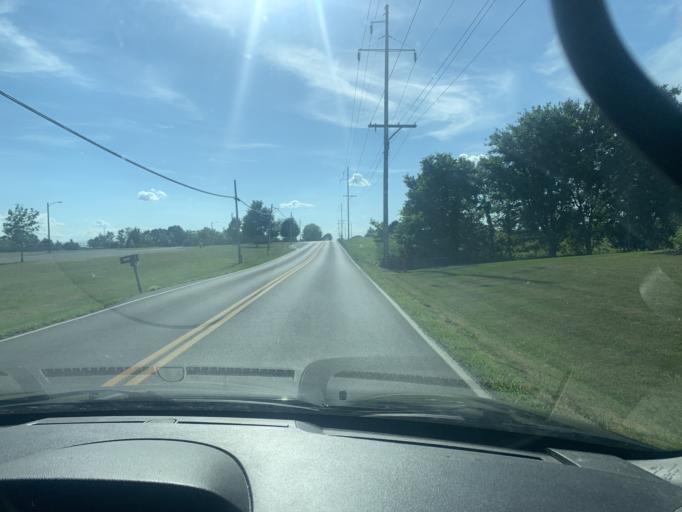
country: US
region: Ohio
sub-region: Logan County
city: Bellefontaine
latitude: 40.3472
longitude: -83.7693
